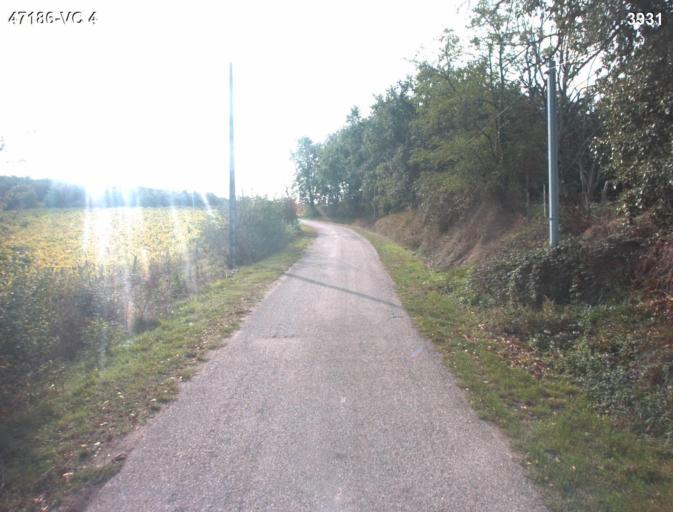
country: FR
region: Aquitaine
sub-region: Departement du Lot-et-Garonne
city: Sainte-Colombe-en-Bruilhois
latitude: 44.1965
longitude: 0.4468
